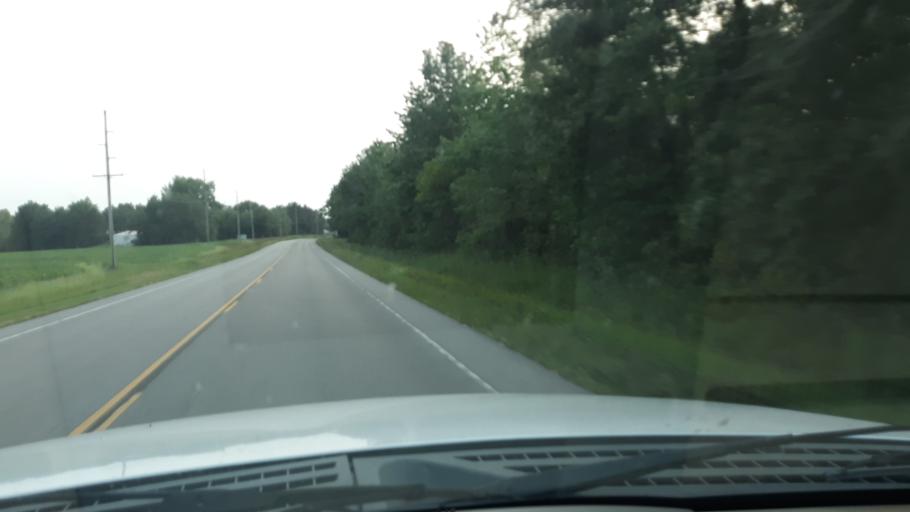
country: US
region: Illinois
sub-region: White County
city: Norris City
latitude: 38.0286
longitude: -88.2577
